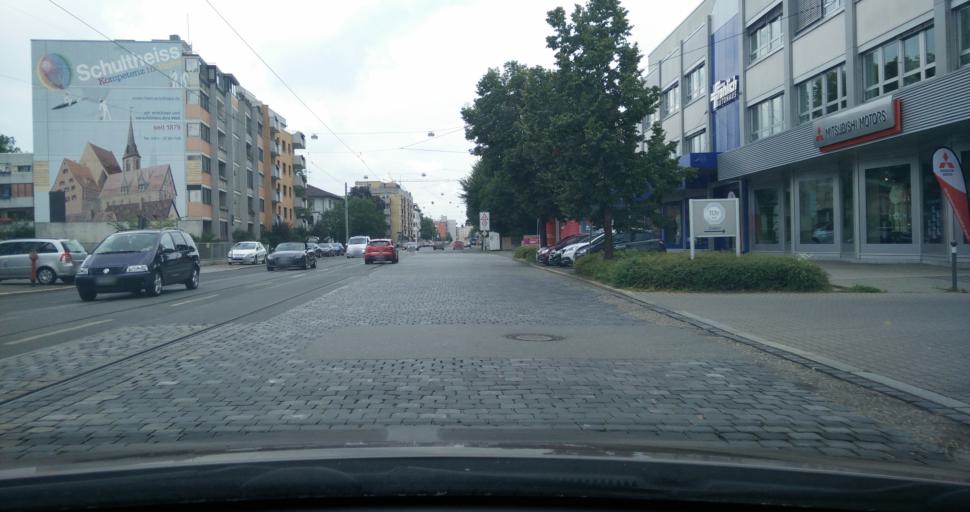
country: DE
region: Bavaria
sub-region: Regierungsbezirk Mittelfranken
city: Nuernberg
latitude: 49.4568
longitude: 11.1220
